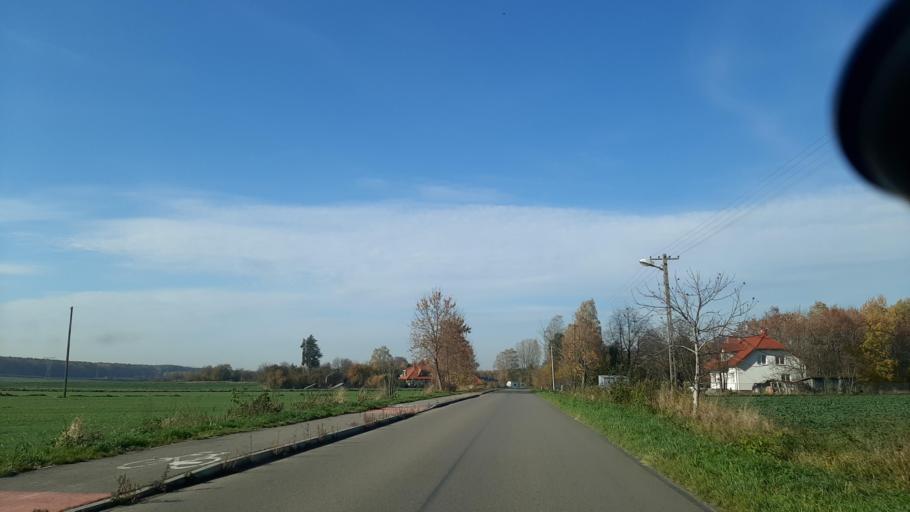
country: PL
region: Lublin Voivodeship
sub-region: Powiat lubelski
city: Jastkow
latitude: 51.3435
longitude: 22.4839
